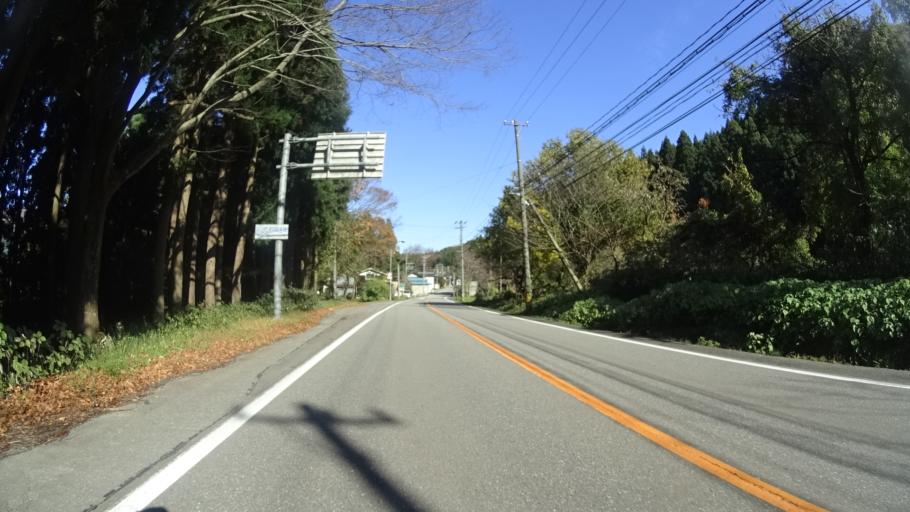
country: JP
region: Ishikawa
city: Tsurugi-asahimachi
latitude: 36.3757
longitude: 136.6147
